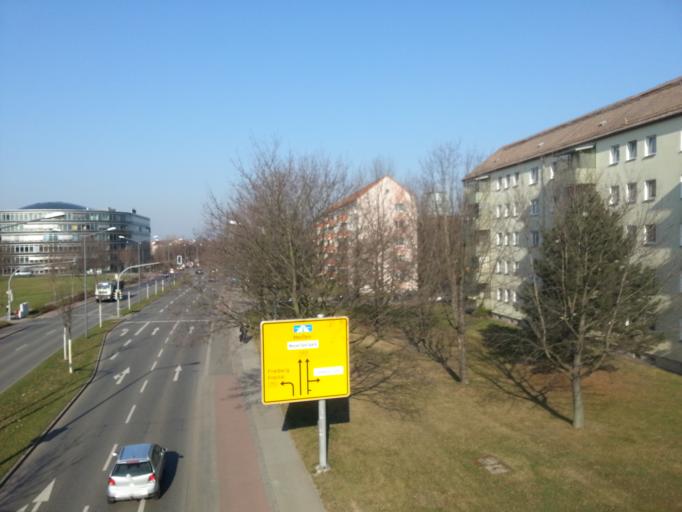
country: DE
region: Saxony
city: Dresden
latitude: 51.0445
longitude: 13.7260
